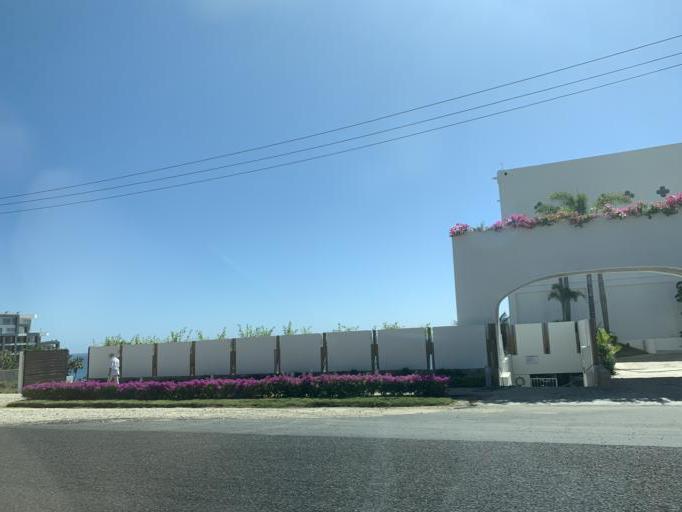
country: MX
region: Baja California Sur
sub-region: Los Cabos
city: San Jose del Cabo
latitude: 22.9693
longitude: -109.7911
